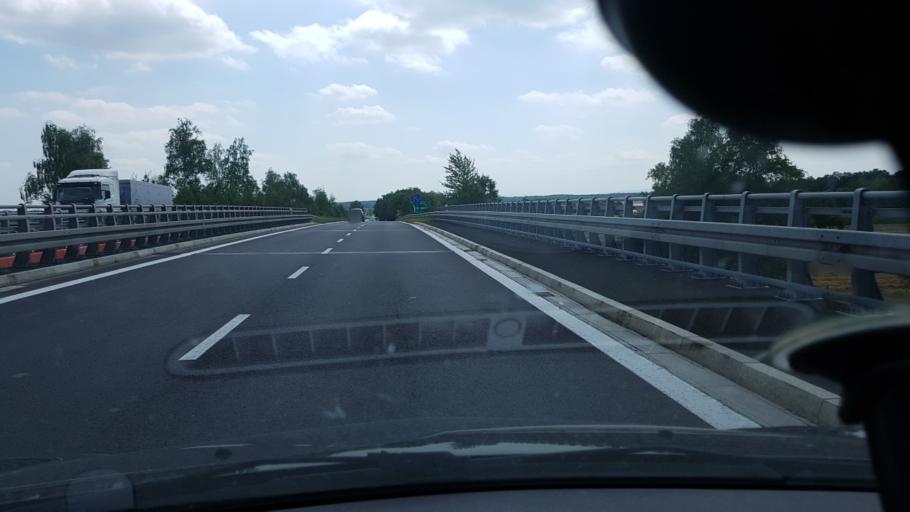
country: PL
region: Silesian Voivodeship
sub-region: Powiat bierunsko-ledzinski
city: Bierun
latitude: 50.1016
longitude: 19.0961
